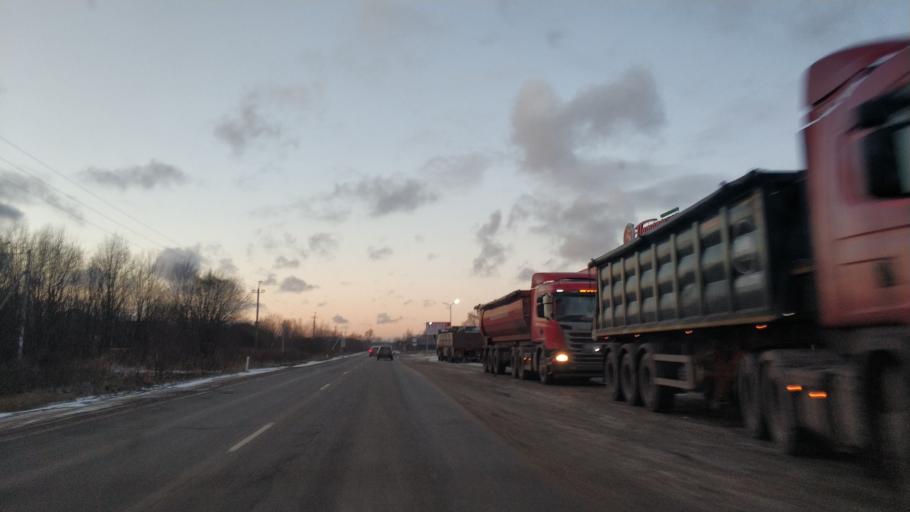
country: RU
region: St.-Petersburg
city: Pontonnyy
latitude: 59.8019
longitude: 30.6328
